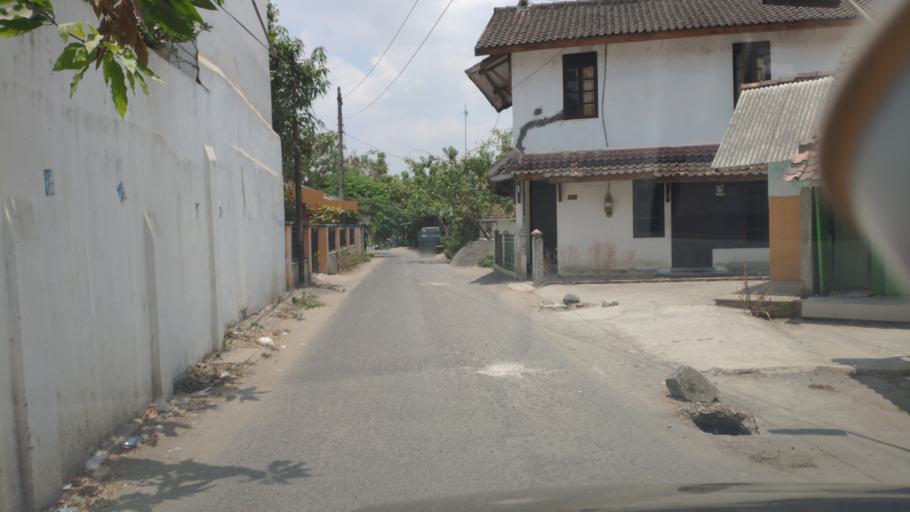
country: ID
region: Central Java
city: Beran
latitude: -6.9789
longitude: 111.4113
